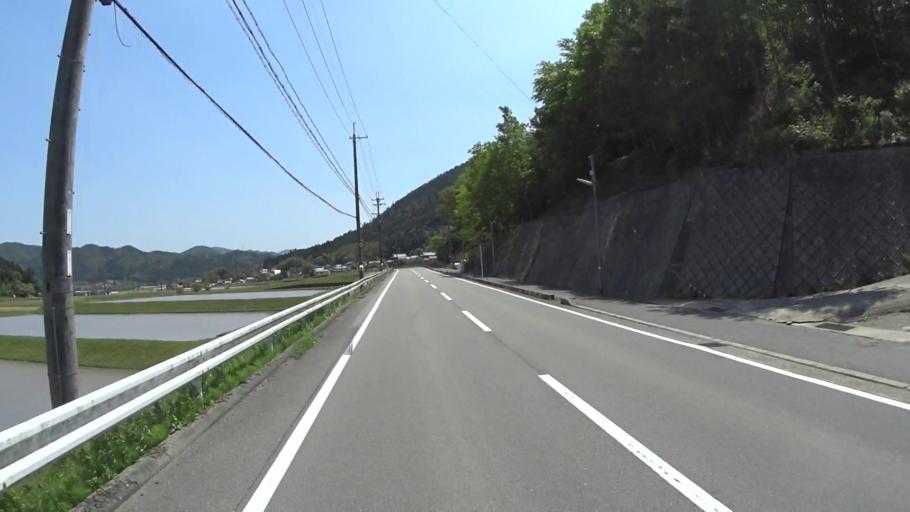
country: JP
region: Kyoto
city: Kameoka
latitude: 35.0302
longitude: 135.4846
